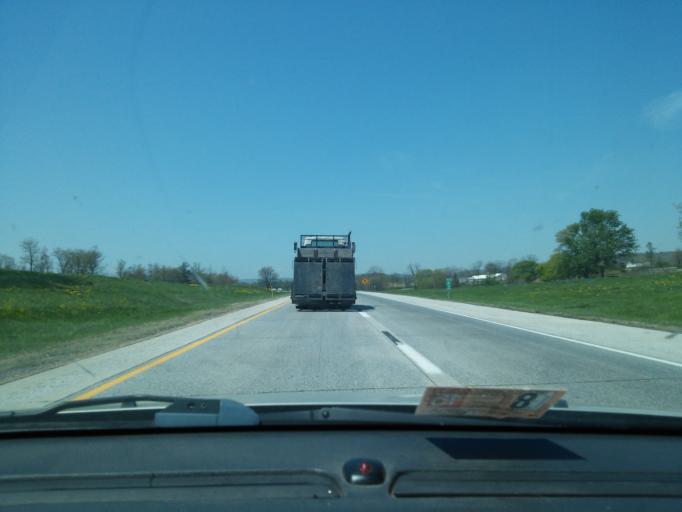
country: US
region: Pennsylvania
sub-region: Lebanon County
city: Fredericksburg
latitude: 40.4522
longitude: -76.4161
